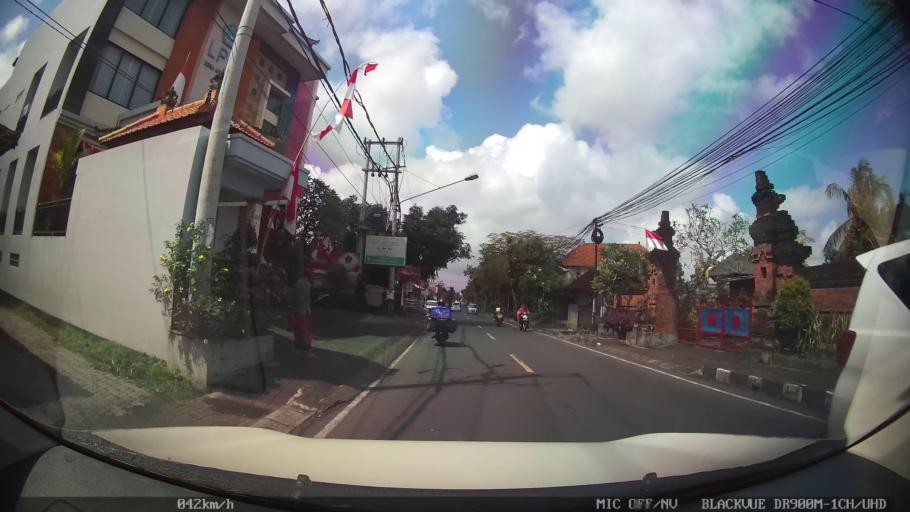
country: ID
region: Bali
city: Banjar Tebongkang
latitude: -8.5479
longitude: 115.2723
